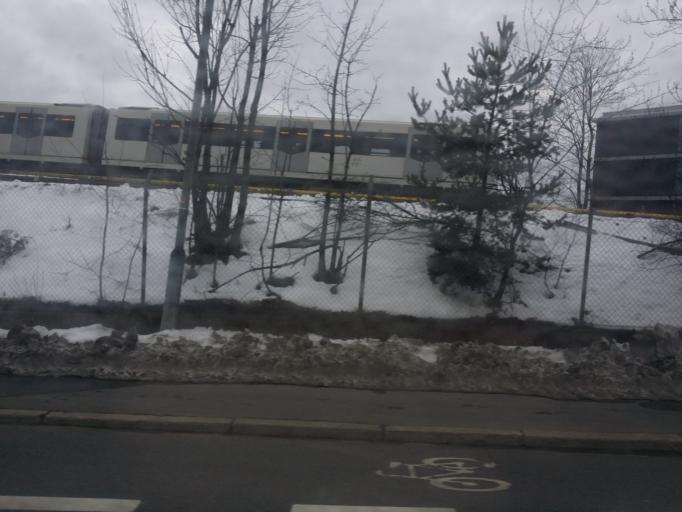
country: NO
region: Oslo
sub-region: Oslo
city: Oslo
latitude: 59.9083
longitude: 10.8162
